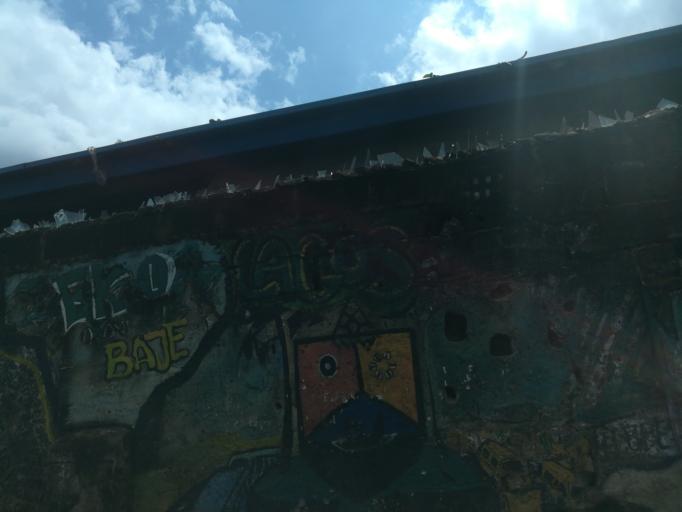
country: NG
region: Lagos
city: Mushin
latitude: 6.5383
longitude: 3.3605
